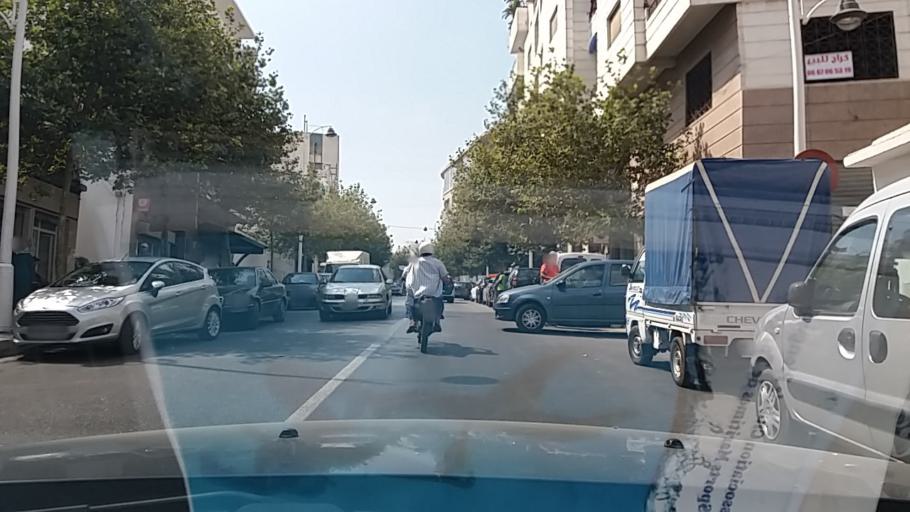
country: MA
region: Tanger-Tetouan
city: Tetouan
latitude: 35.5712
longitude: -5.3606
